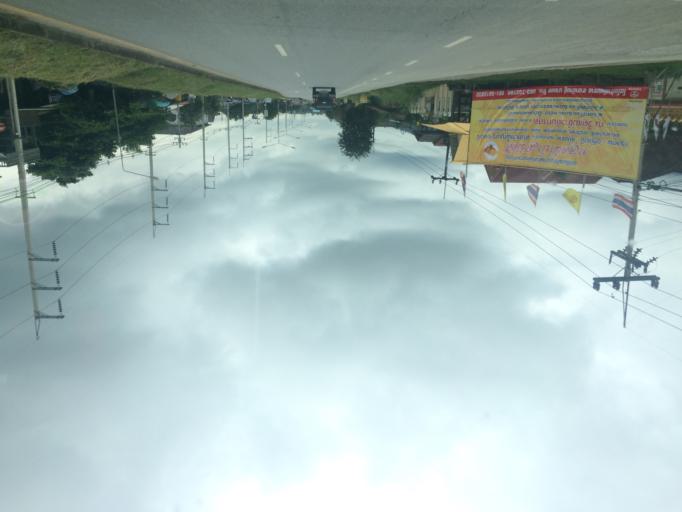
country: TH
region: Chiang Rai
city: Mae Chan
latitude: 20.0750
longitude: 99.8756
